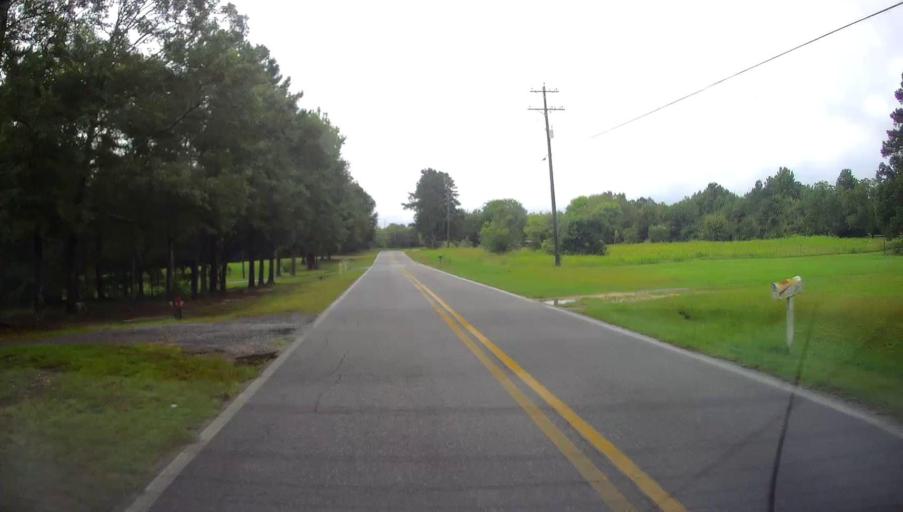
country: US
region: Georgia
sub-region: Bibb County
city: West Point
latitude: 32.8007
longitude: -83.8259
